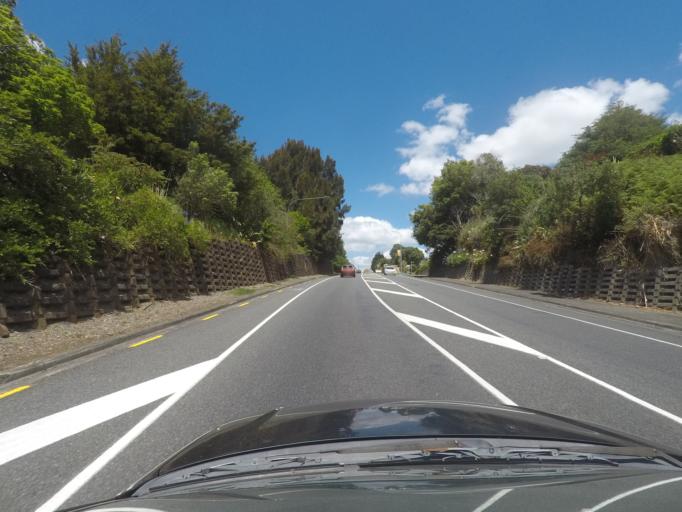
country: NZ
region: Northland
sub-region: Whangarei
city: Whangarei
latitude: -35.7436
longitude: 174.3660
